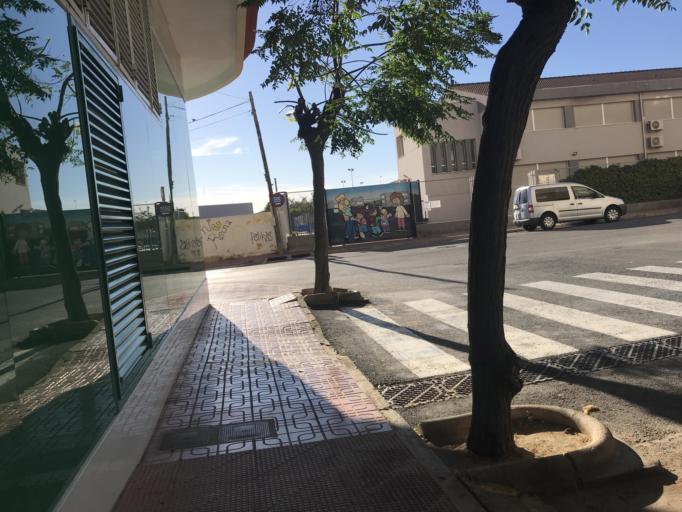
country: ES
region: Valencia
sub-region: Provincia de Alicante
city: Torrevieja
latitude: 37.9799
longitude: -0.6905
